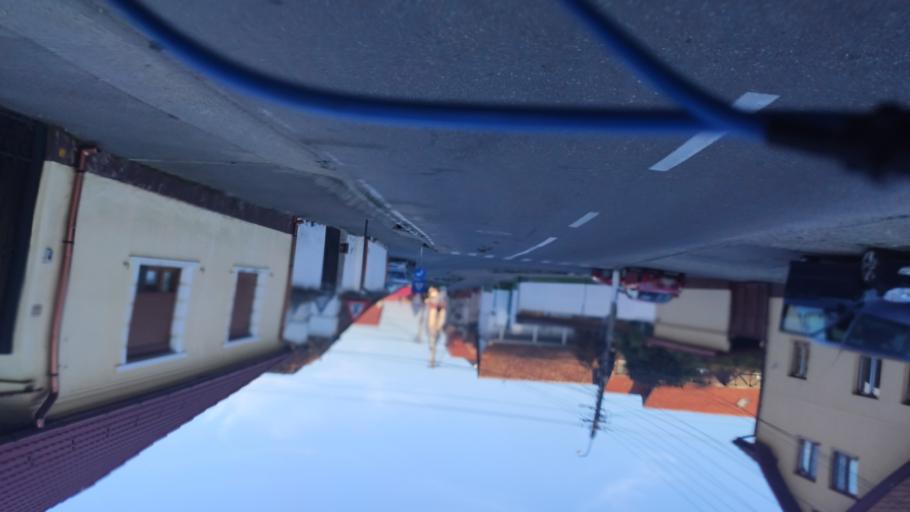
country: RO
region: Brasov
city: Codlea
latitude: 45.6957
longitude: 25.4429
